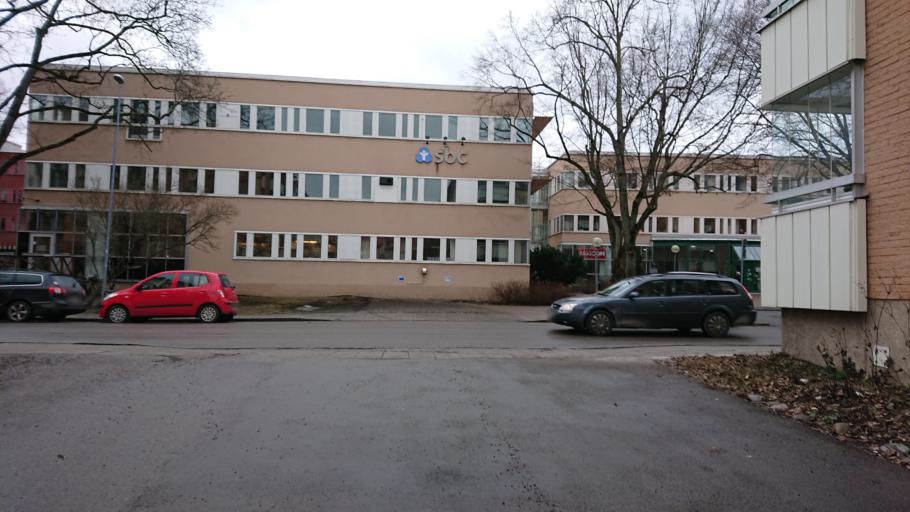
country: SE
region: Uppsala
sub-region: Uppsala Kommun
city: Uppsala
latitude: 59.8541
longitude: 17.6460
